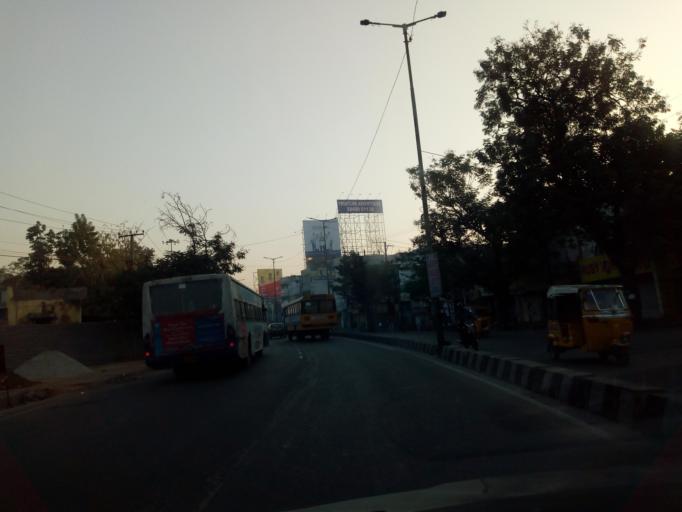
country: IN
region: Telangana
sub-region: Rangareddi
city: Gaddi Annaram
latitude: 17.3953
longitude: 78.5022
